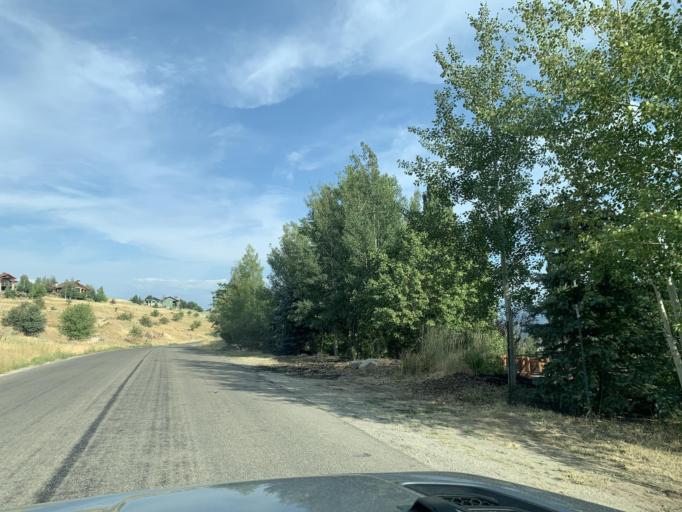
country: US
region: Utah
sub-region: Weber County
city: Wolf Creek
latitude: 41.3289
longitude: -111.8195
